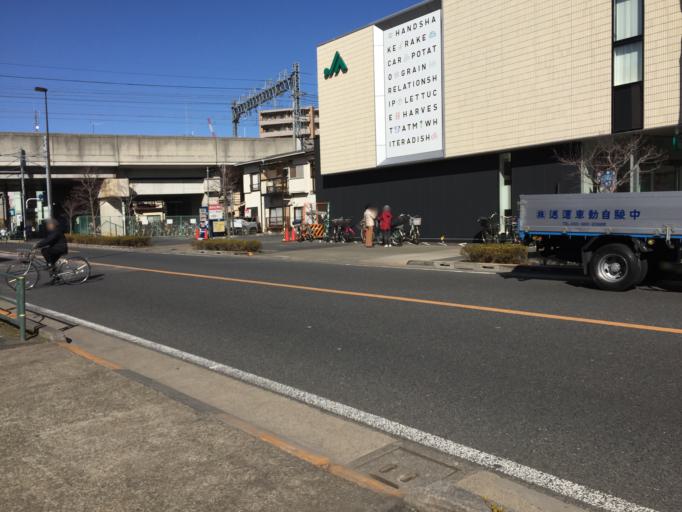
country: JP
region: Tokyo
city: Chofugaoka
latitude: 35.6332
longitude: 139.5795
